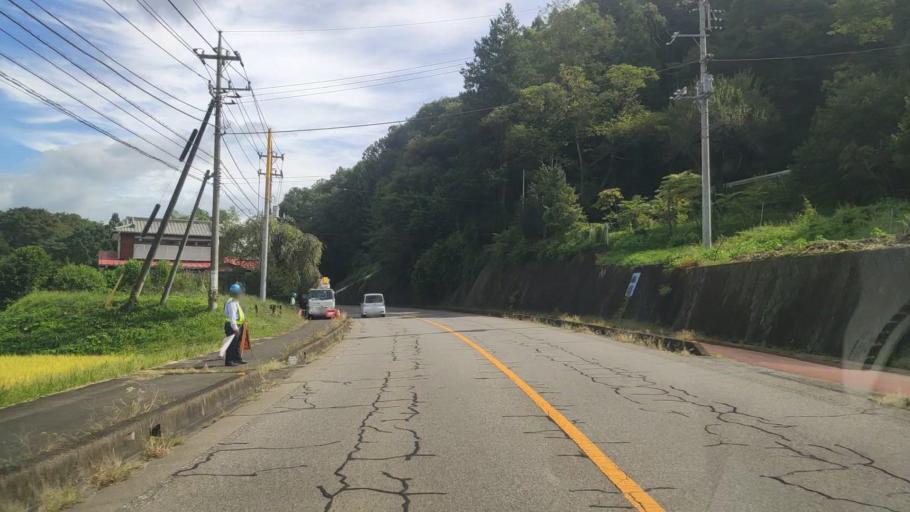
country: JP
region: Gunma
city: Nakanojomachi
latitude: 36.6111
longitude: 138.8844
